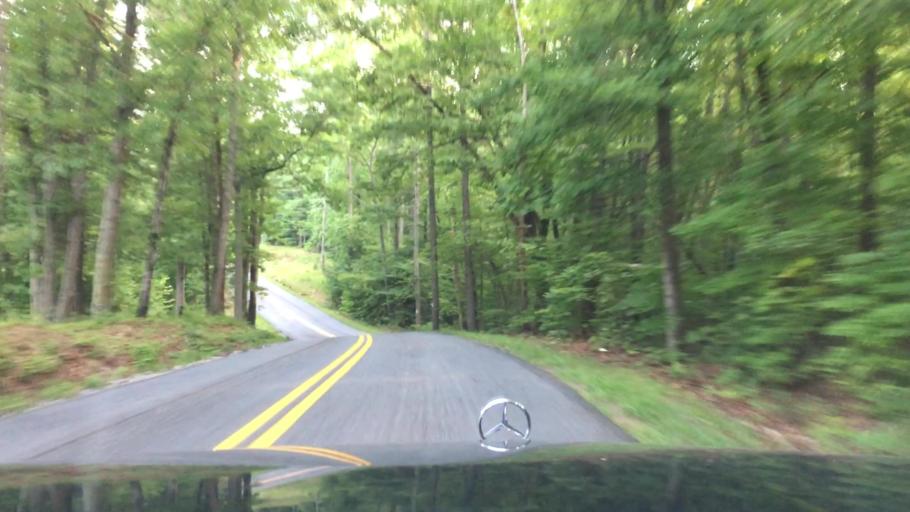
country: US
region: Virginia
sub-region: Campbell County
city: Timberlake
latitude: 37.2683
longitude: -79.2642
